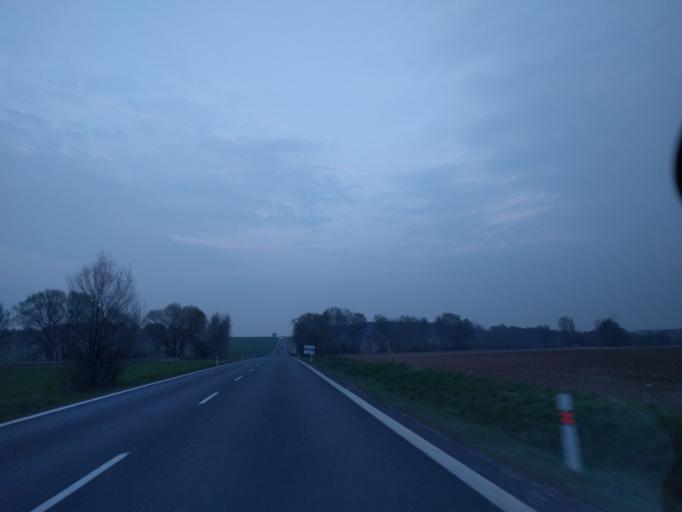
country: CZ
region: Central Bohemia
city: Rakovnik
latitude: 50.1688
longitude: 13.6587
